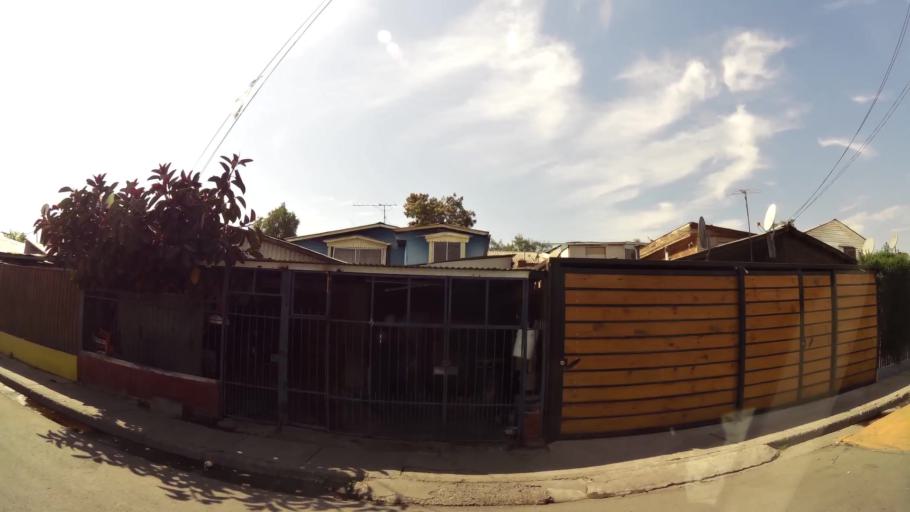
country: CL
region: Santiago Metropolitan
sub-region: Provincia de Santiago
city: La Pintana
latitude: -33.5611
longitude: -70.6489
